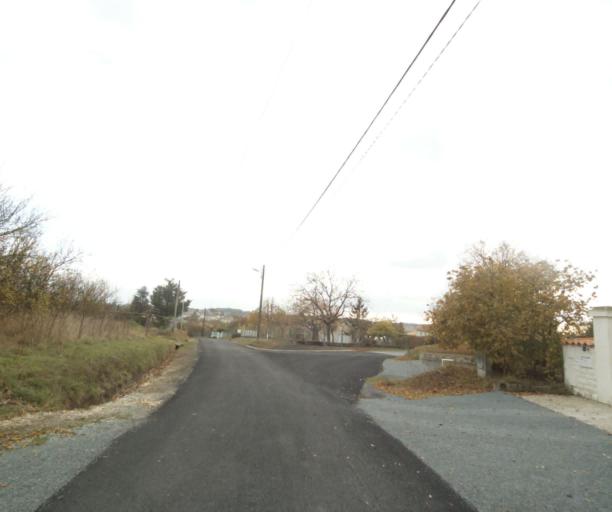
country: FR
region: Poitou-Charentes
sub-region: Departement de la Charente-Maritime
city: Saint-Georges-des-Coteaux
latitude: 45.7697
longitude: -0.7155
